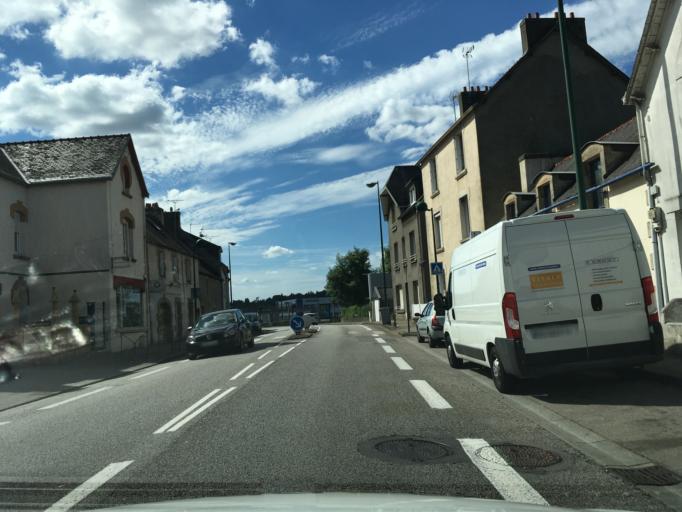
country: FR
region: Brittany
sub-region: Departement du Finistere
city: Quimper
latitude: 47.9919
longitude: -4.0770
